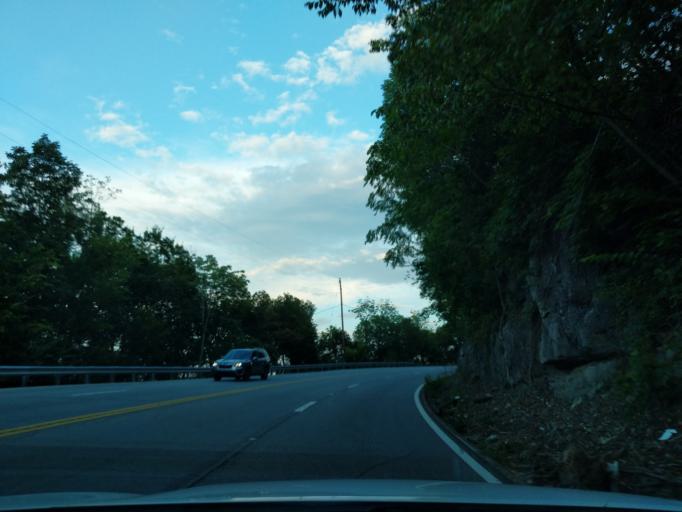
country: US
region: Tennessee
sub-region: Hamilton County
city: Lookout Mountain
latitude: 35.0240
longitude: -85.3430
